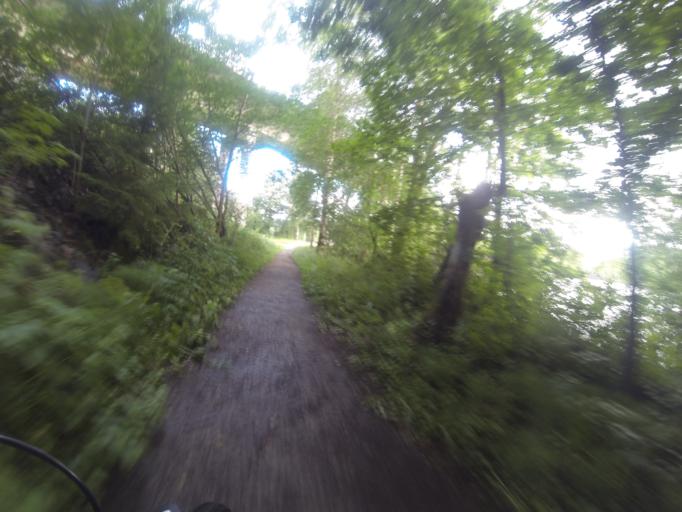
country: SE
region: Dalarna
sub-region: Avesta Kommun
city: Avesta
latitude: 60.1493
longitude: 16.1998
